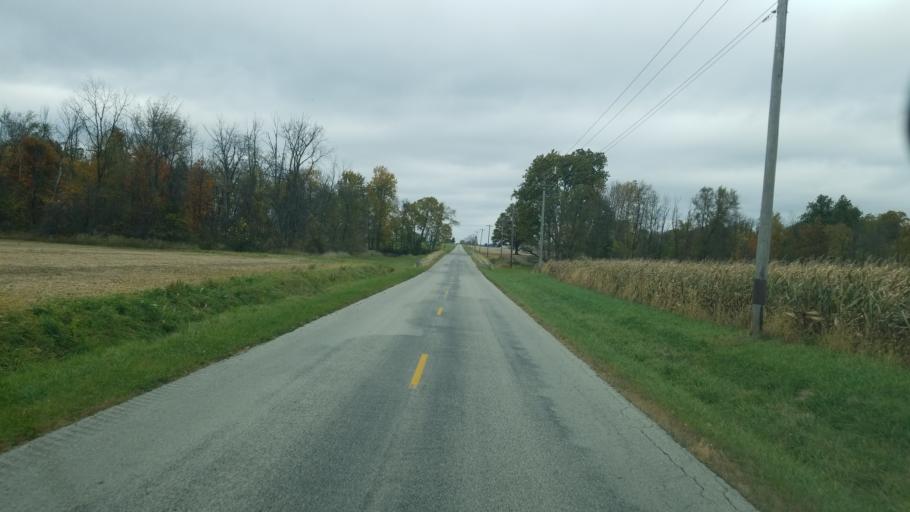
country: US
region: Ohio
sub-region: Sandusky County
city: Mount Carmel
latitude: 41.0706
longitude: -82.9575
